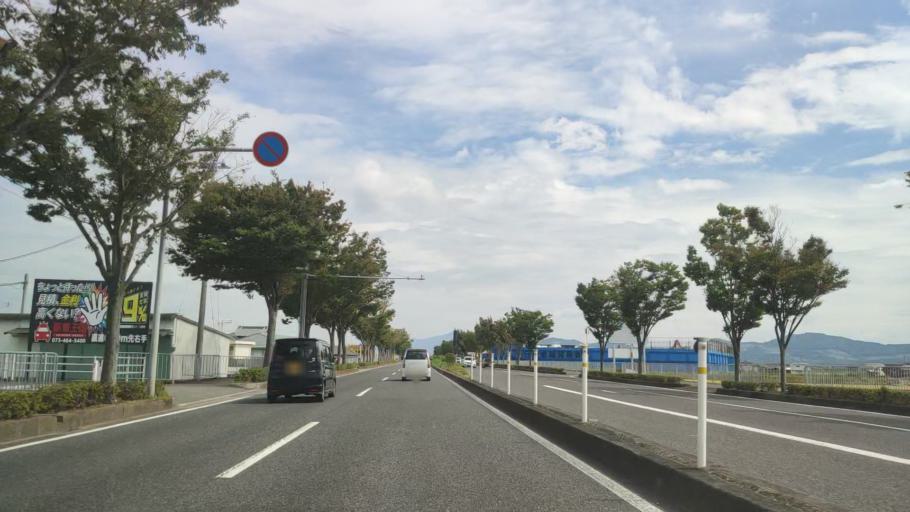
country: JP
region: Wakayama
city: Iwade
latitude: 34.2553
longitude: 135.2398
